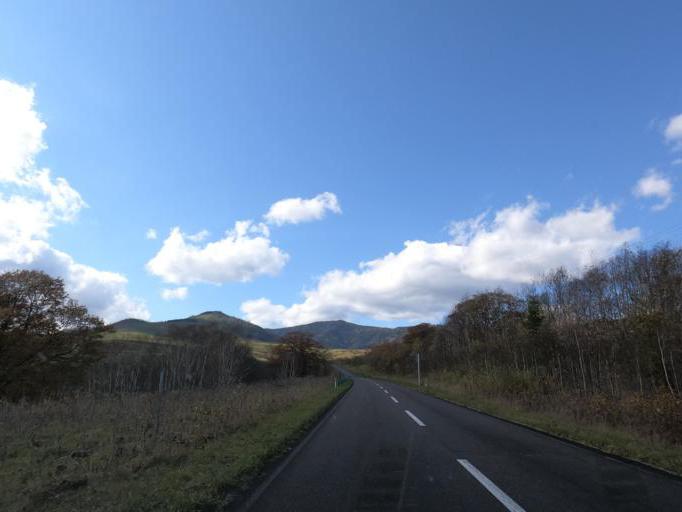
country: JP
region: Hokkaido
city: Otofuke
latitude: 43.2911
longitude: 143.2051
